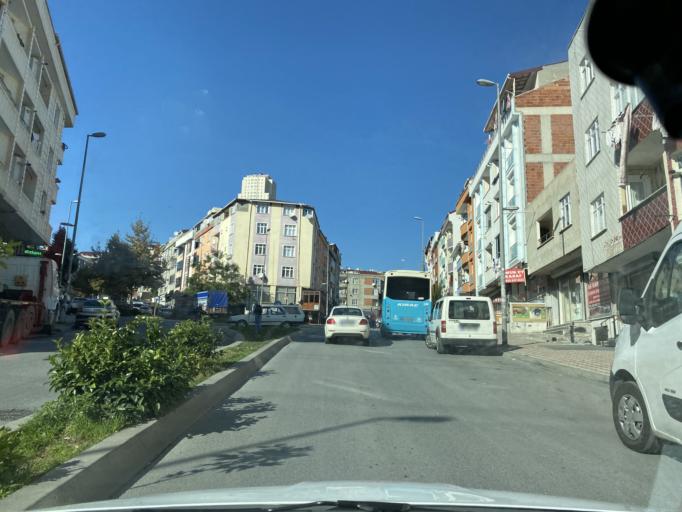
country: TR
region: Istanbul
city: Esenyurt
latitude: 41.0285
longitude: 28.6522
